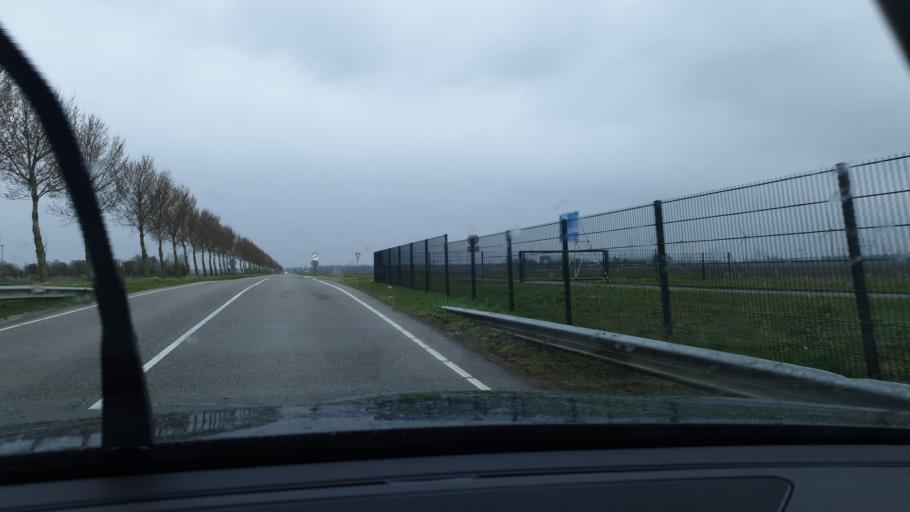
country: NL
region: Flevoland
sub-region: Gemeente Lelystad
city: Lelystad
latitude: 52.5477
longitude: 5.5678
